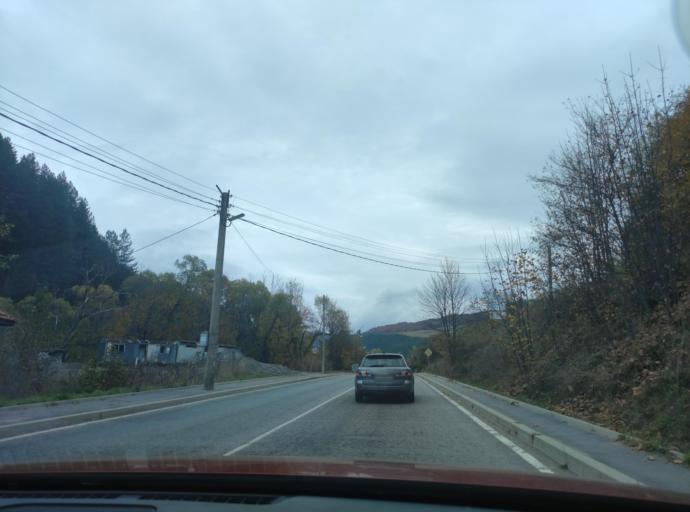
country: BG
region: Sofiya
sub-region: Obshtina Godech
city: Godech
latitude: 43.0734
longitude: 23.1083
